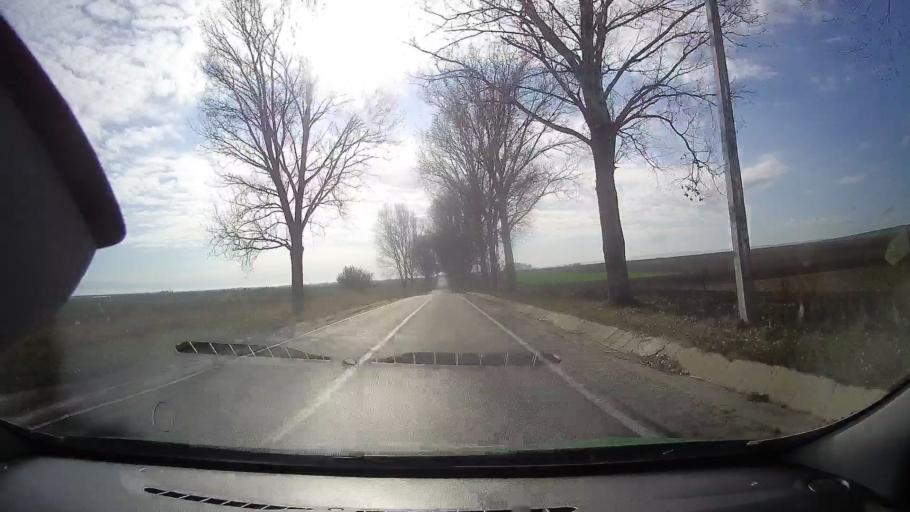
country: RO
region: Tulcea
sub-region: Comuna Valea Nucarilor
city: Agighiol
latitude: 45.0035
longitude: 28.8855
